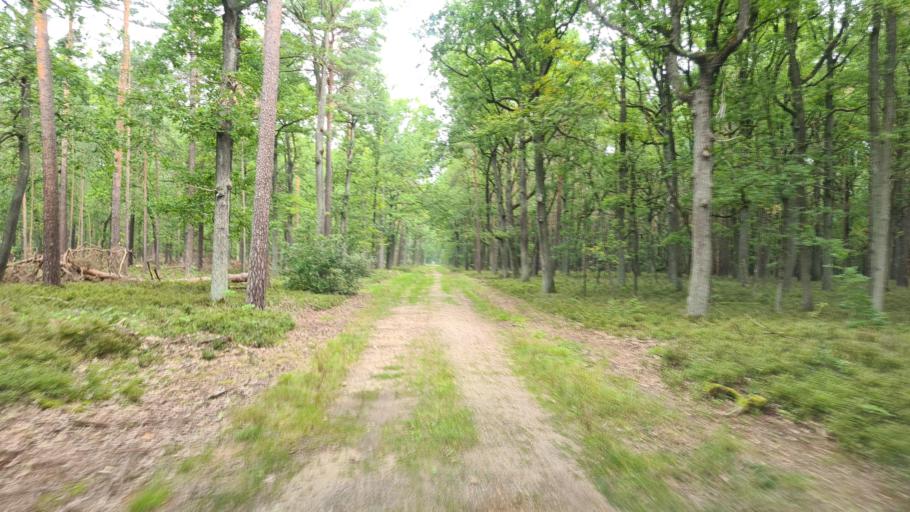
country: DE
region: Brandenburg
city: Hohenbucko
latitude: 51.7788
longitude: 13.5481
